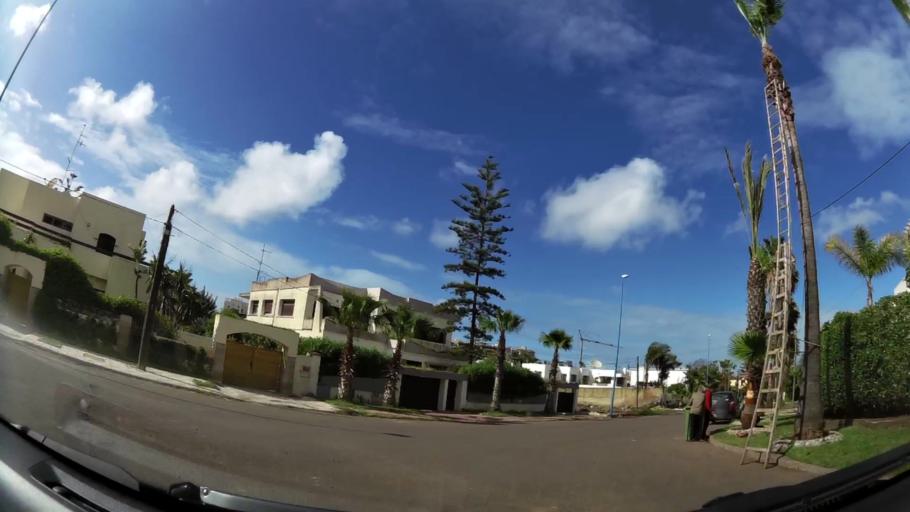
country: MA
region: Grand Casablanca
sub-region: Casablanca
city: Casablanca
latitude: 33.5502
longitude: -7.6296
